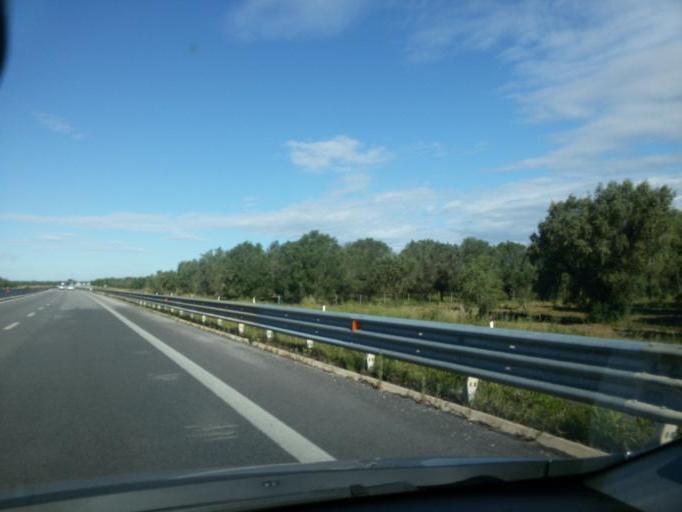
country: IT
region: Apulia
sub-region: Provincia di Brindisi
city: Latiano
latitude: 40.5649
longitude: 17.7605
